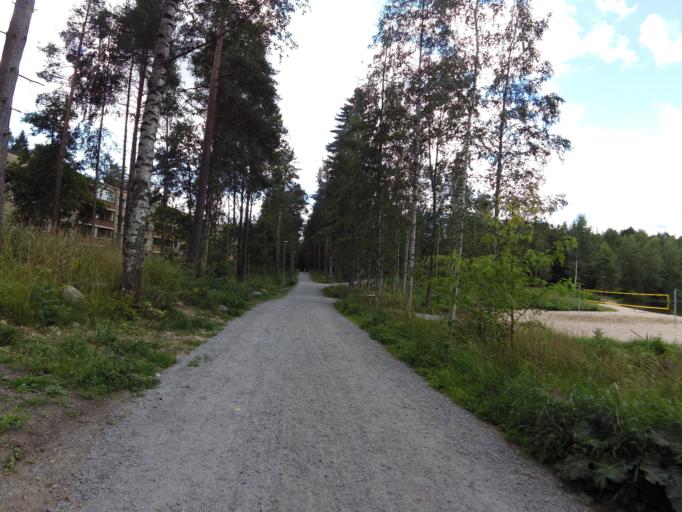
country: FI
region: Pirkanmaa
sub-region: Tampere
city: Pirkkala
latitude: 61.5070
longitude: 23.6151
